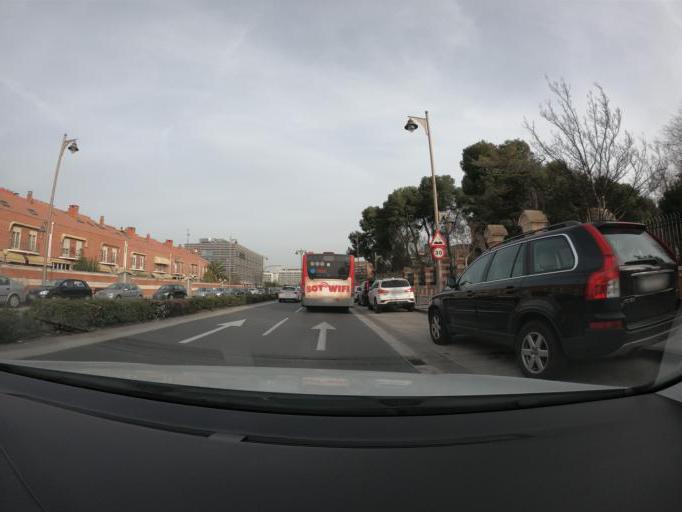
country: ES
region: La Rioja
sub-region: Provincia de La Rioja
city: Logrono
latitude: 42.4622
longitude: -2.4258
